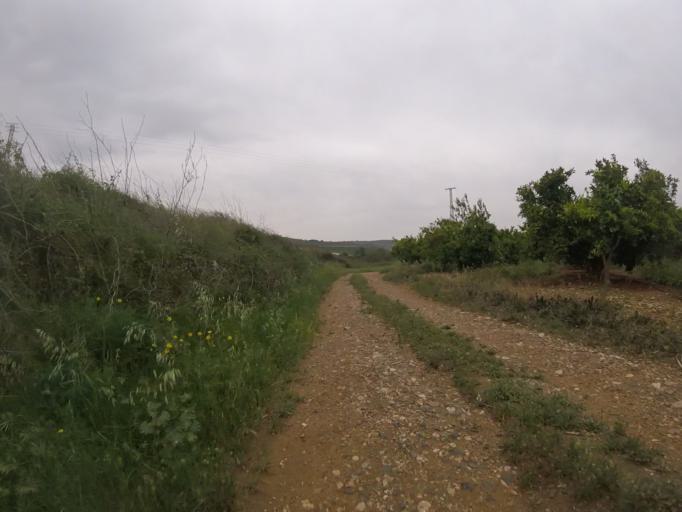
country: ES
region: Valencia
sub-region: Provincia de Castello
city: Alcoceber
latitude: 40.2676
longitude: 0.2570
